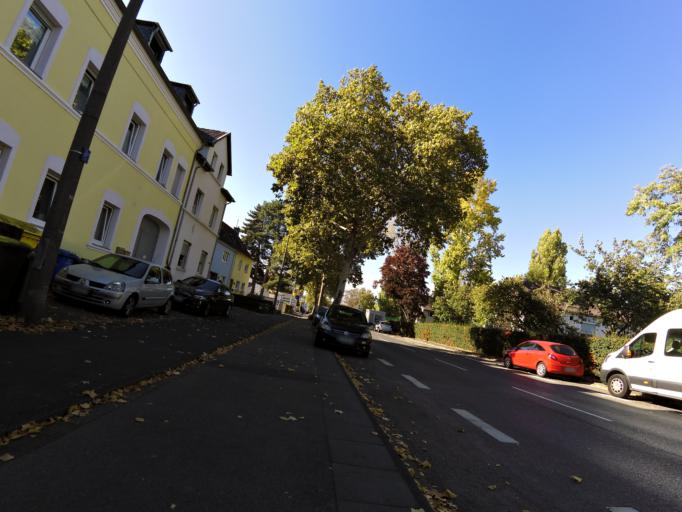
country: DE
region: North Rhine-Westphalia
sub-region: Regierungsbezirk Koln
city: Alfter
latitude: 50.7143
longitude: 7.0411
